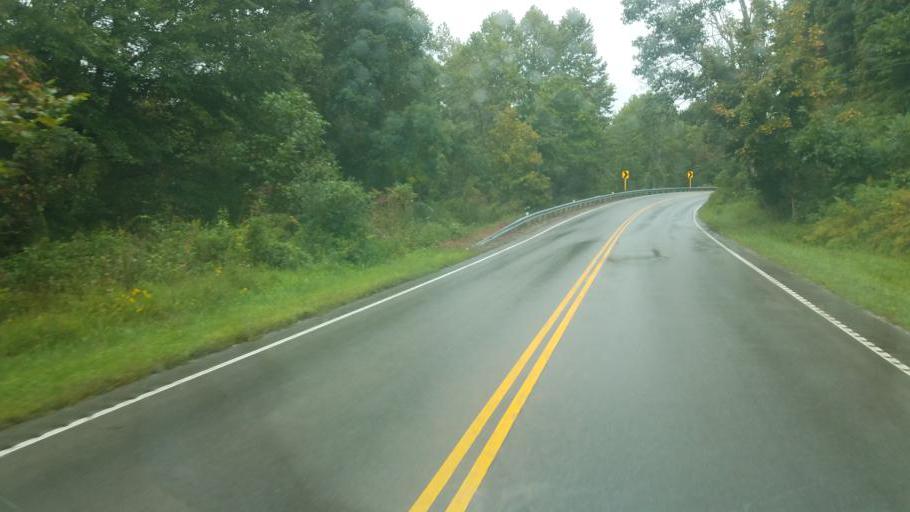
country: US
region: Ohio
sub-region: Jackson County
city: Oak Hill
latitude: 38.8251
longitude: -82.6630
